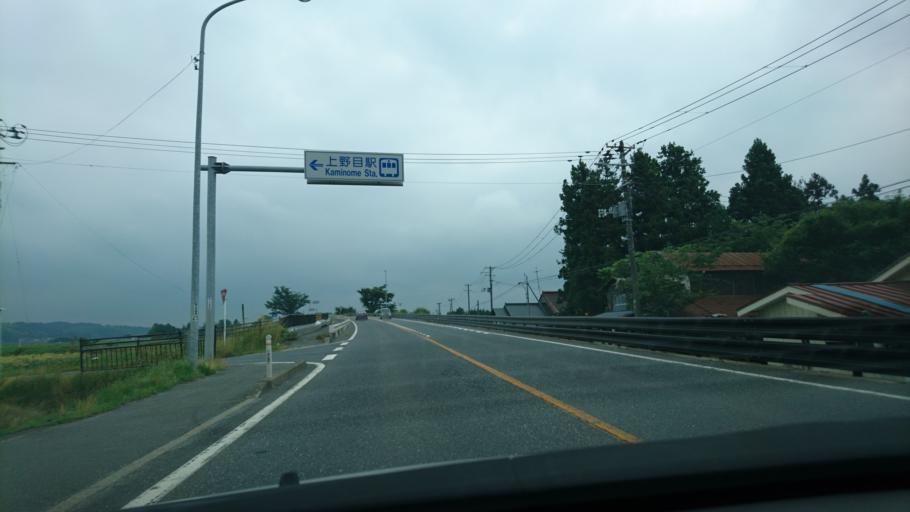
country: JP
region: Miyagi
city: Furukawa
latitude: 38.6797
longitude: 140.8585
